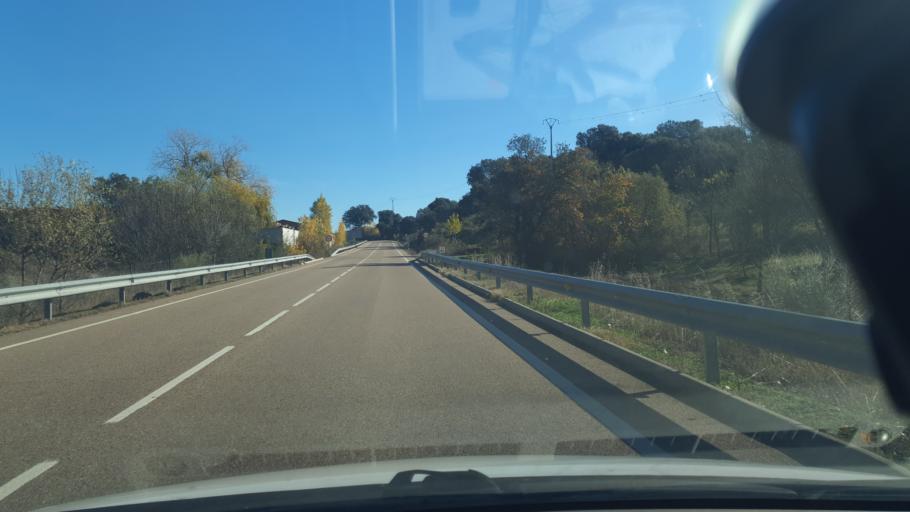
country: ES
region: Castille and Leon
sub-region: Provincia de Avila
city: Arenas de San Pedro
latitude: 40.1793
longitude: -5.0456
